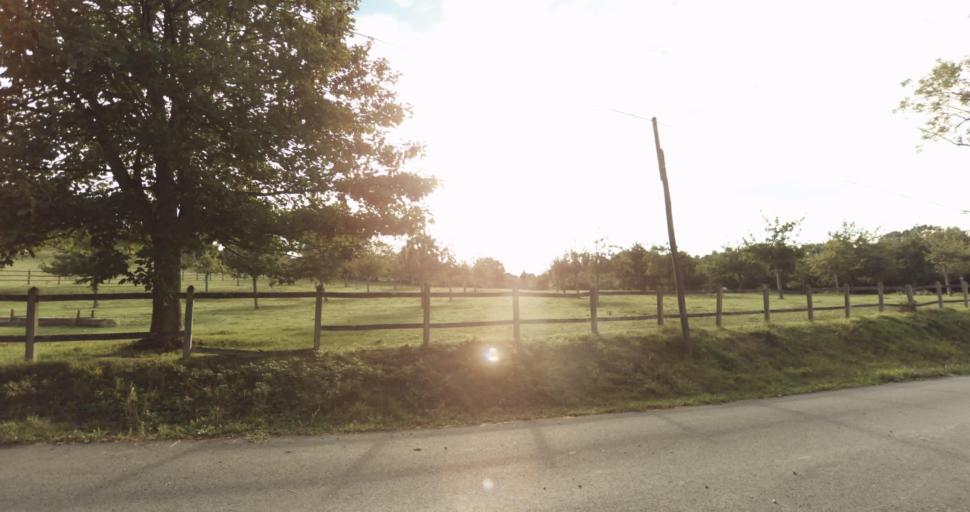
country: FR
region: Lower Normandy
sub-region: Departement de l'Orne
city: Vimoutiers
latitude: 48.8818
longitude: 0.2242
